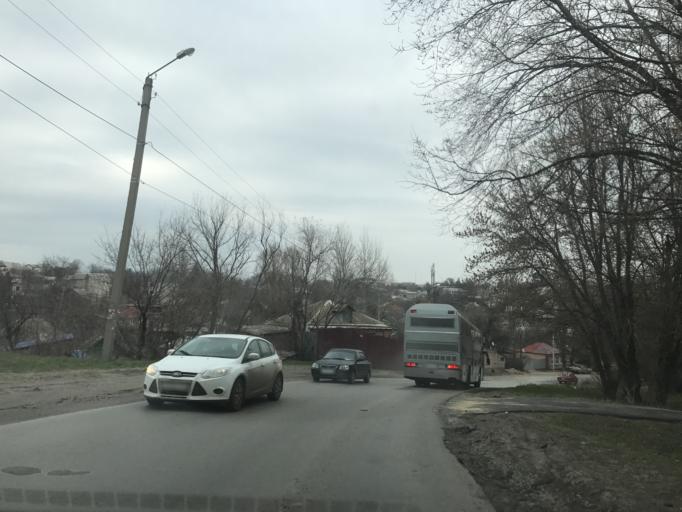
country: RU
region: Rostov
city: Novocherkassk
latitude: 47.4036
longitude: 40.0783
